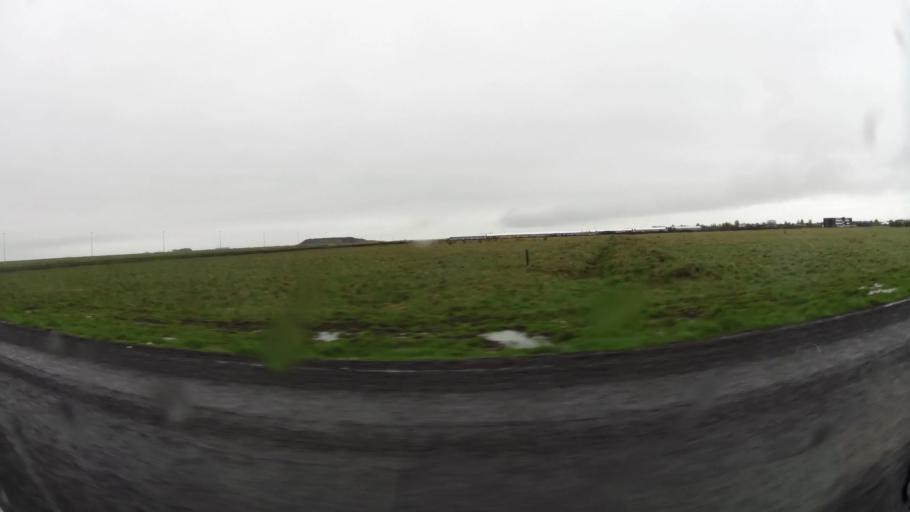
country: IS
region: South
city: Selfoss
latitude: 63.9292
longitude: -20.9707
